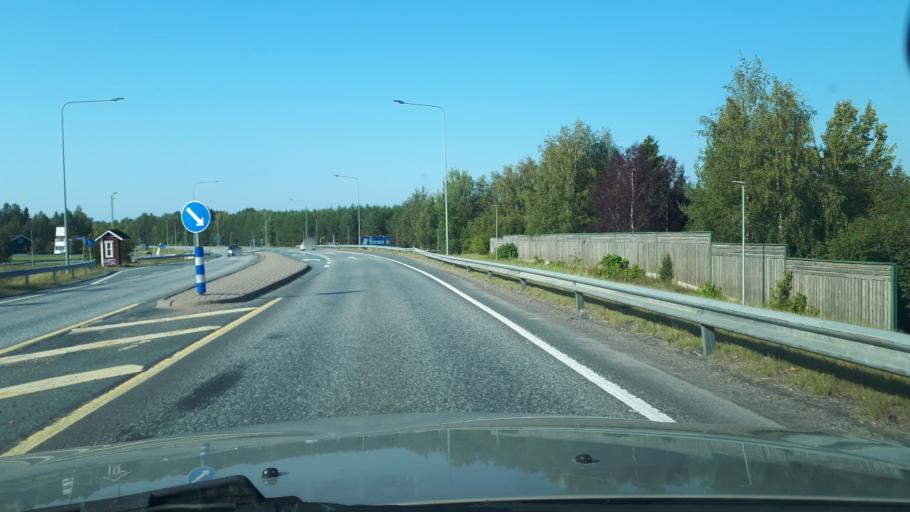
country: FI
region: Northern Ostrobothnia
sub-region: Oulunkaari
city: Ii
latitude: 65.3320
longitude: 25.3766
